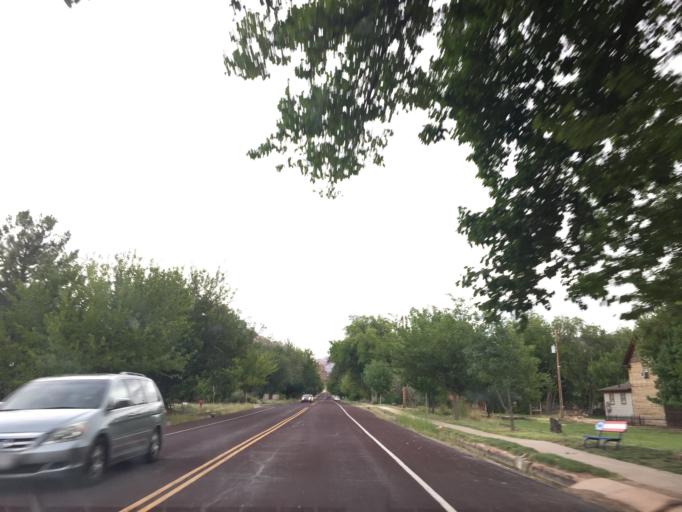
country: US
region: Utah
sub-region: Washington County
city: Hildale
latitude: 37.1610
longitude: -113.0463
